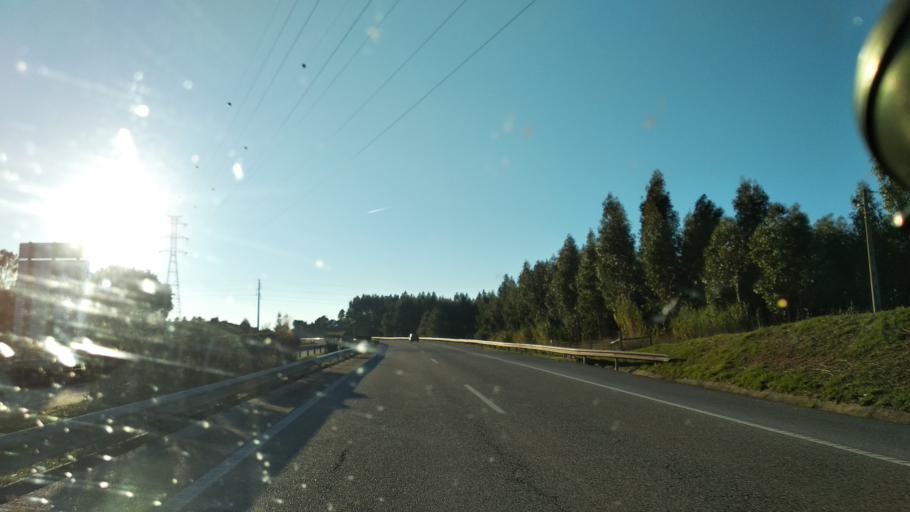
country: PT
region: Santarem
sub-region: Entroncamento
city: Entroncamento
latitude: 39.4860
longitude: -8.4710
